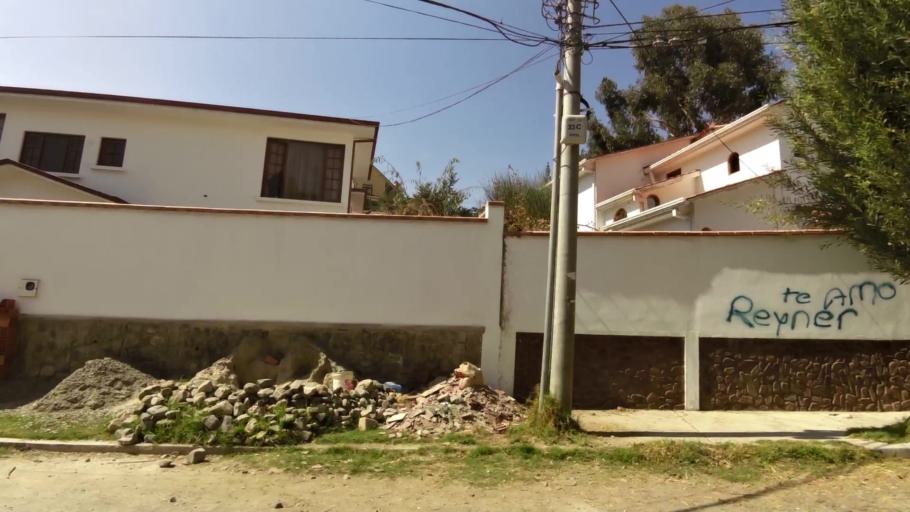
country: BO
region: La Paz
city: La Paz
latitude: -16.5429
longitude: -68.0670
